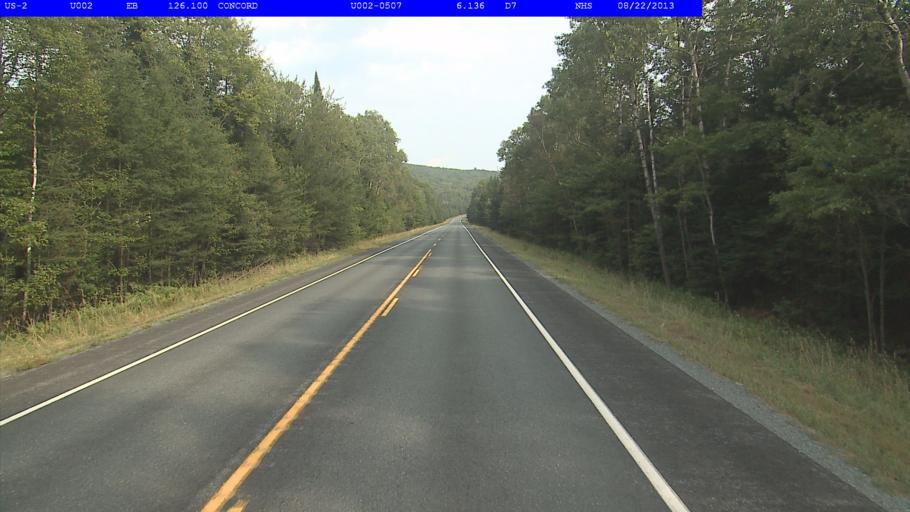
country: US
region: Vermont
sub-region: Caledonia County
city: Lyndonville
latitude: 44.4673
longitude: -71.8437
